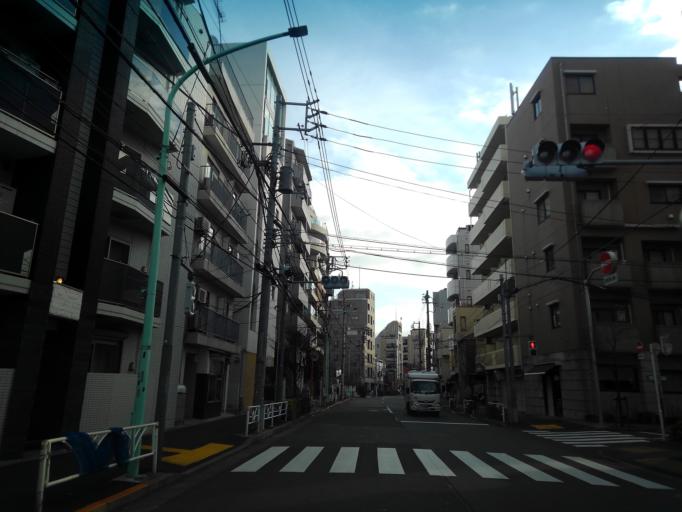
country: JP
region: Tokyo
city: Tokyo
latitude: 35.6641
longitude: 139.6787
